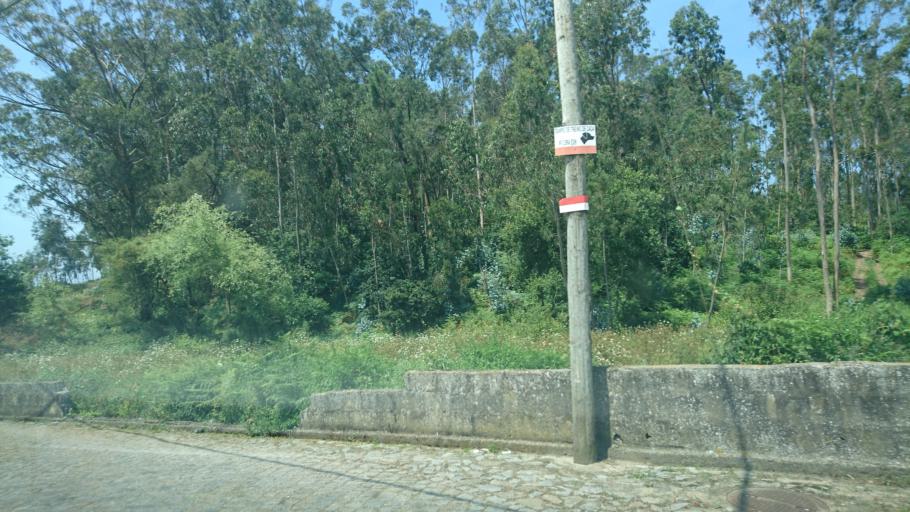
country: PT
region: Porto
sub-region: Matosinhos
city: Lavra
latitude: 41.2713
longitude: -8.7193
